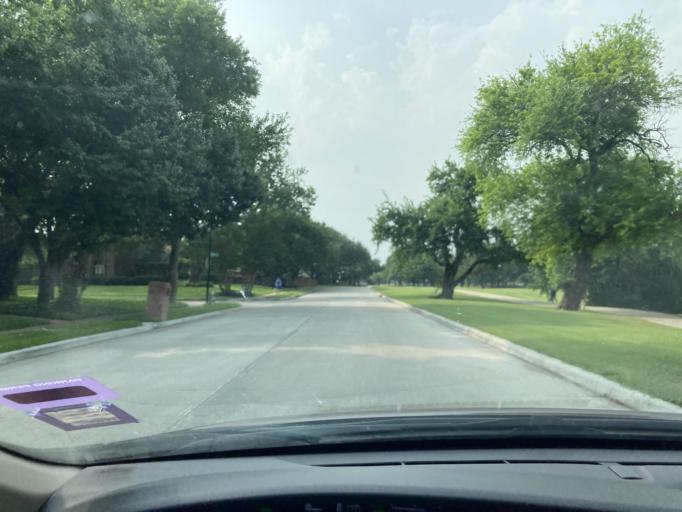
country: US
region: Texas
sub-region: Collin County
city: Plano
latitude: 33.0523
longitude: -96.7274
